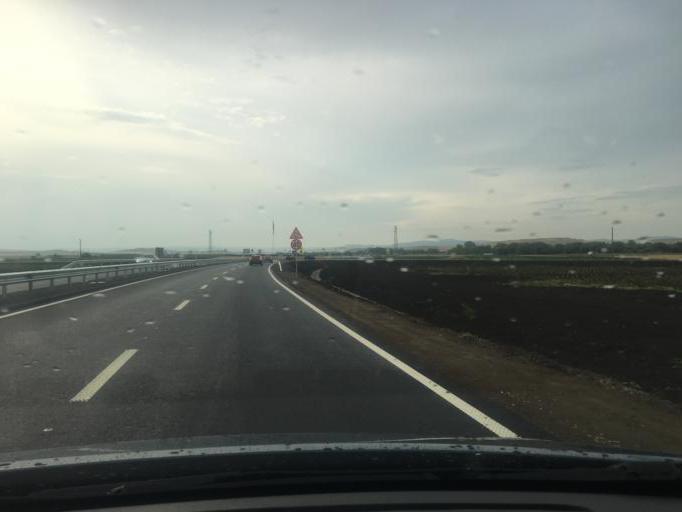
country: BG
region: Burgas
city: Aheloy
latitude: 42.6438
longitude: 27.6374
